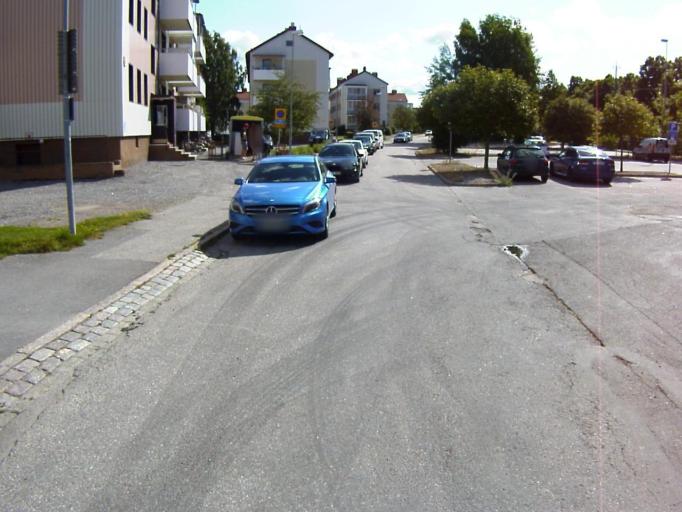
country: SE
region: Soedermanland
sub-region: Eskilstuna Kommun
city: Eskilstuna
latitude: 59.3657
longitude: 16.5240
